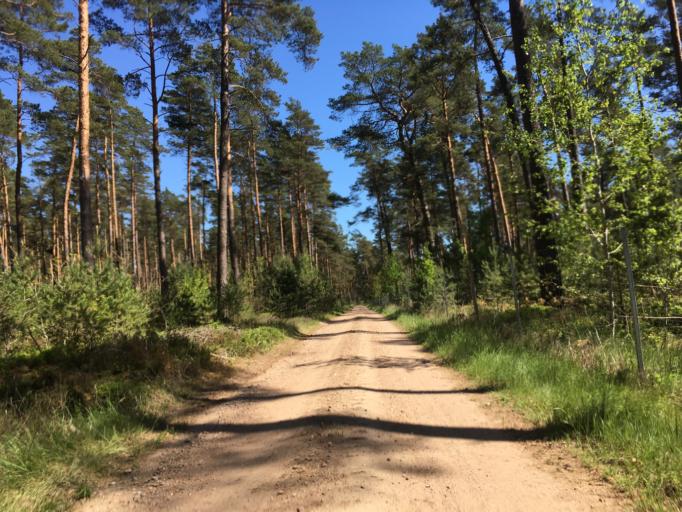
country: DE
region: Brandenburg
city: Friedrichswalde
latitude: 52.9854
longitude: 13.6131
